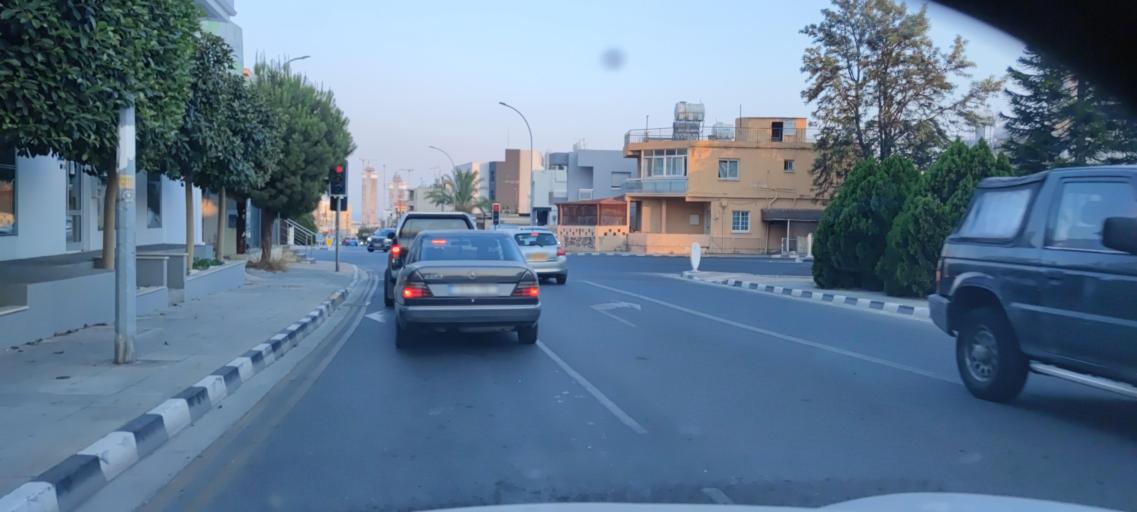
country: CY
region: Limassol
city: Limassol
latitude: 34.6987
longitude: 33.0475
